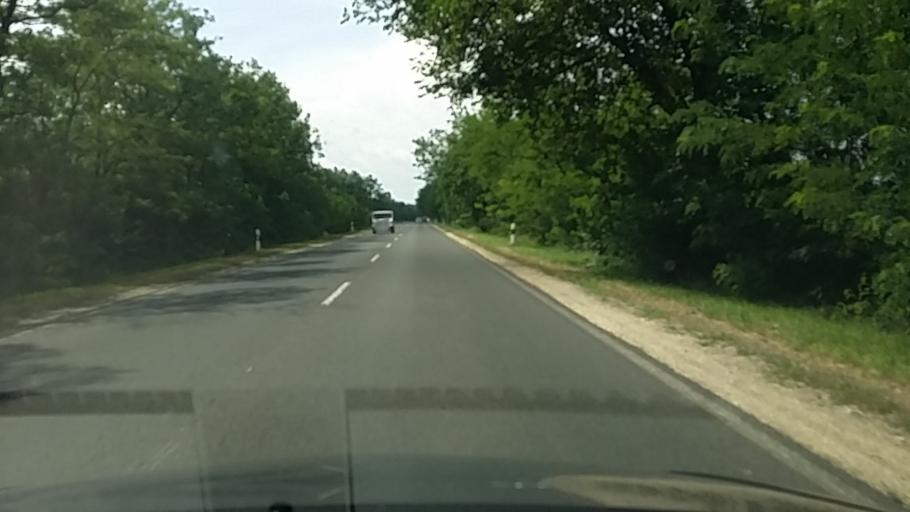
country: HU
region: Pest
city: Taborfalva
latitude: 47.1018
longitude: 19.4676
